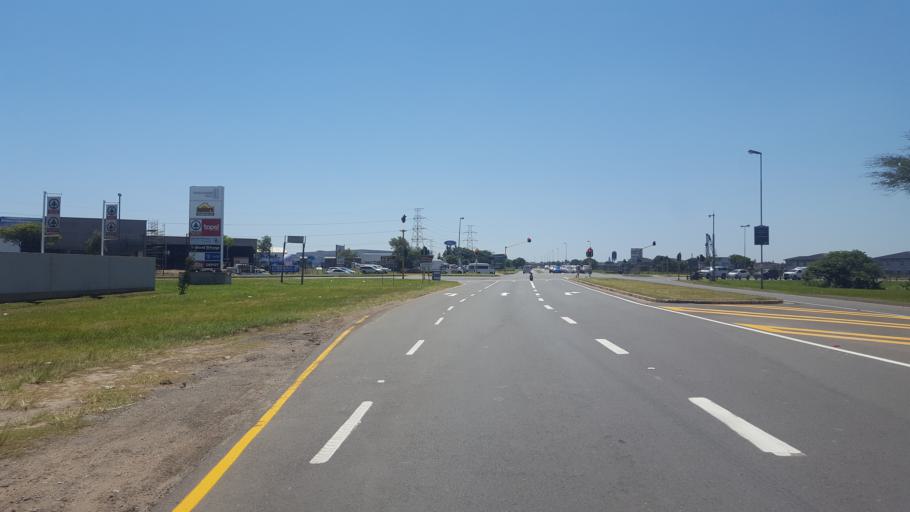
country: ZA
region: KwaZulu-Natal
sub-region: uThungulu District Municipality
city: Richards Bay
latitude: -28.7456
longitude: 32.0516
